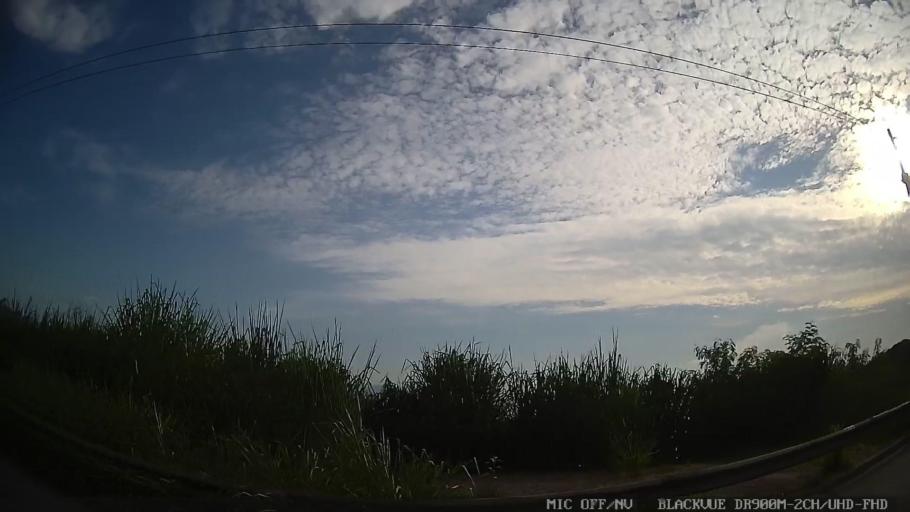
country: BR
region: Sao Paulo
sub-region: Sao Sebastiao
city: Sao Sebastiao
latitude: -23.7260
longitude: -45.4090
